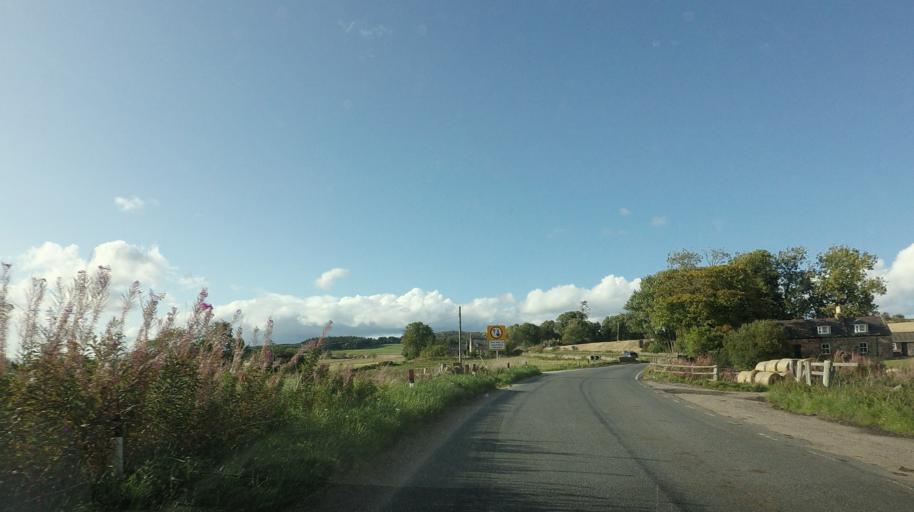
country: GB
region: Scotland
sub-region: Aberdeenshire
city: Kemnay
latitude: 57.1352
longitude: -2.4296
